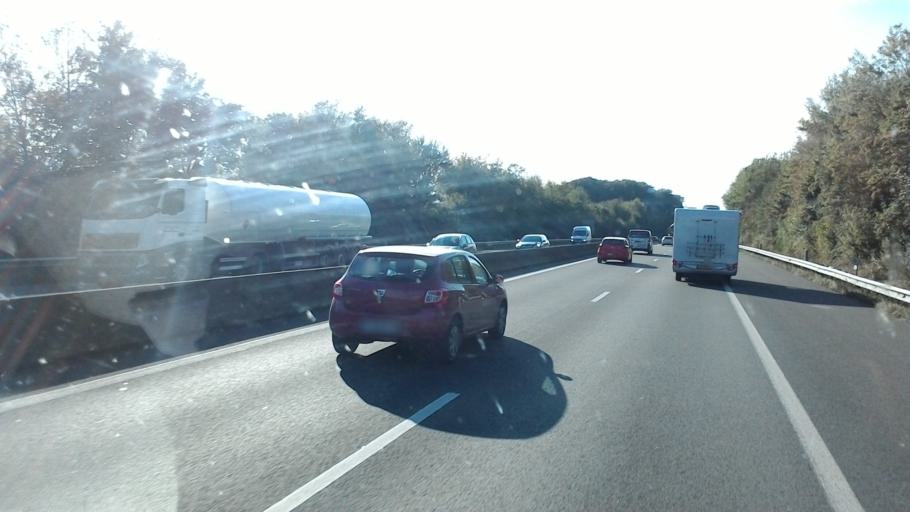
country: LU
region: Luxembourg
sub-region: Canton de Luxembourg
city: Strassen
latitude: 49.6305
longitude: 6.0569
